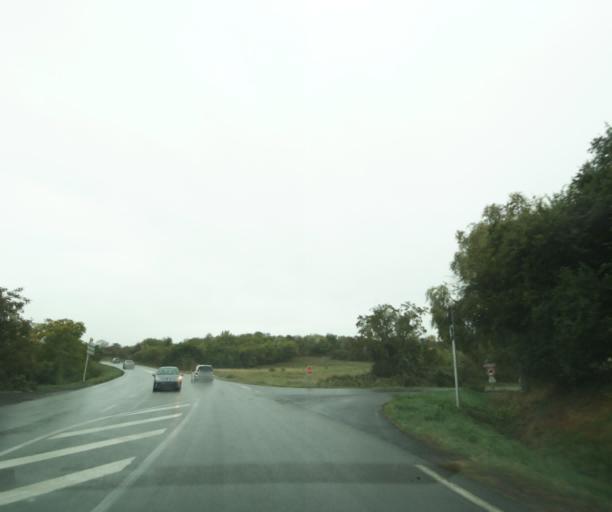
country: FR
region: Auvergne
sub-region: Departement du Puy-de-Dome
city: Cebazat
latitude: 45.8435
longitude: 3.1074
